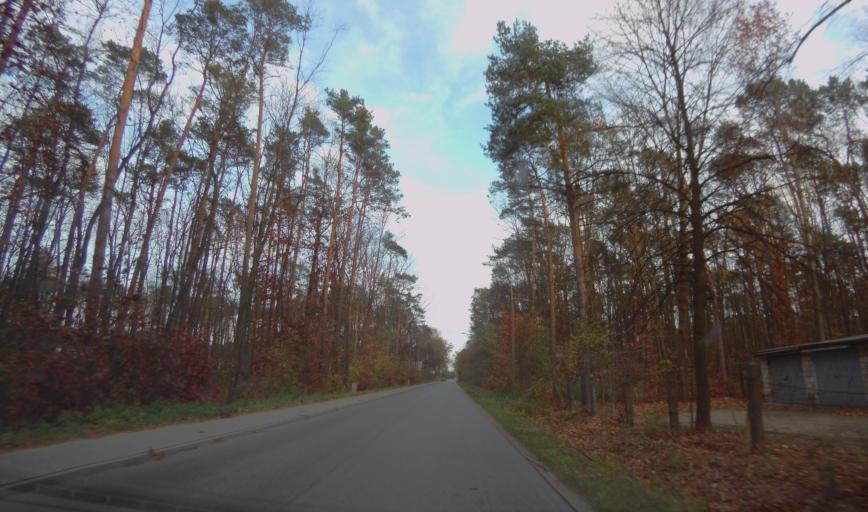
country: PL
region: Subcarpathian Voivodeship
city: Nowa Sarzyna
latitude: 50.3311
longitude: 22.3264
